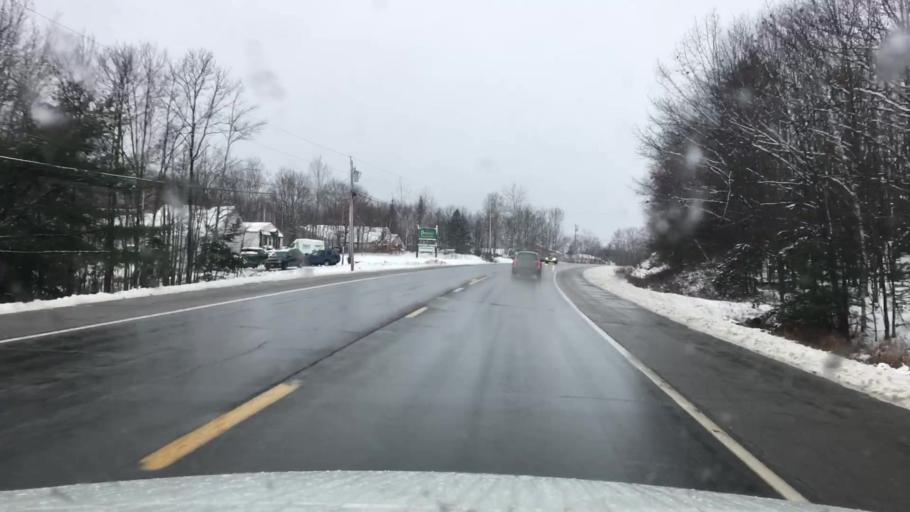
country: US
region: Maine
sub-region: Knox County
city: Rockland
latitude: 44.1683
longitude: -69.1585
